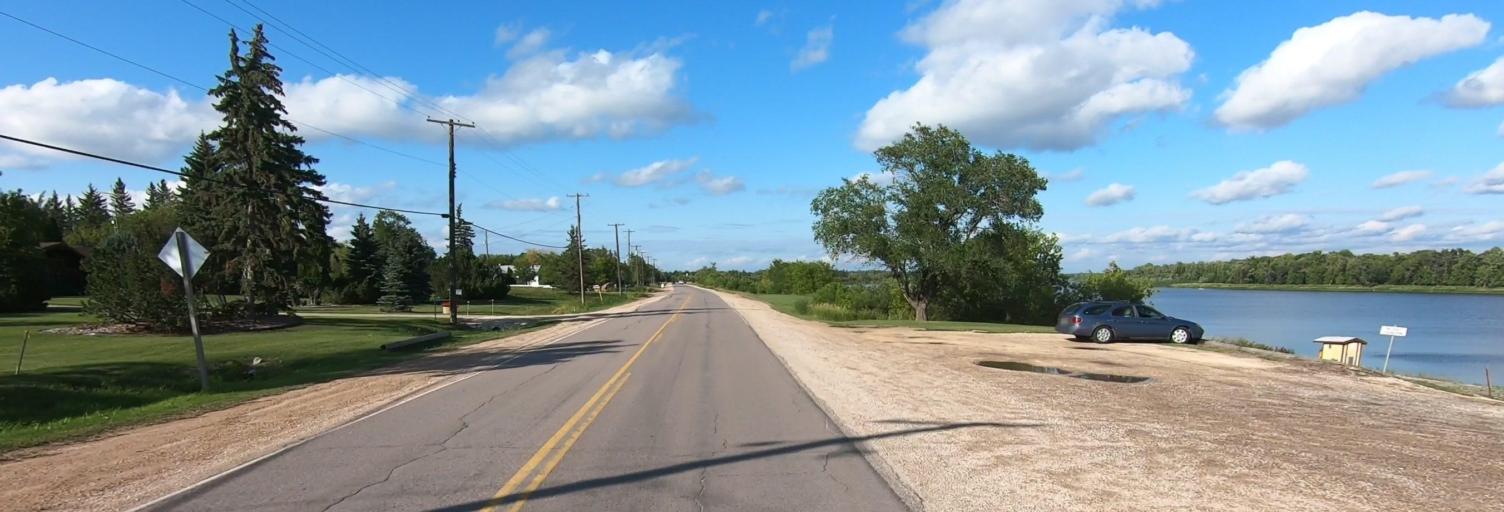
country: CA
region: Manitoba
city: Selkirk
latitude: 50.1698
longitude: -96.8625
